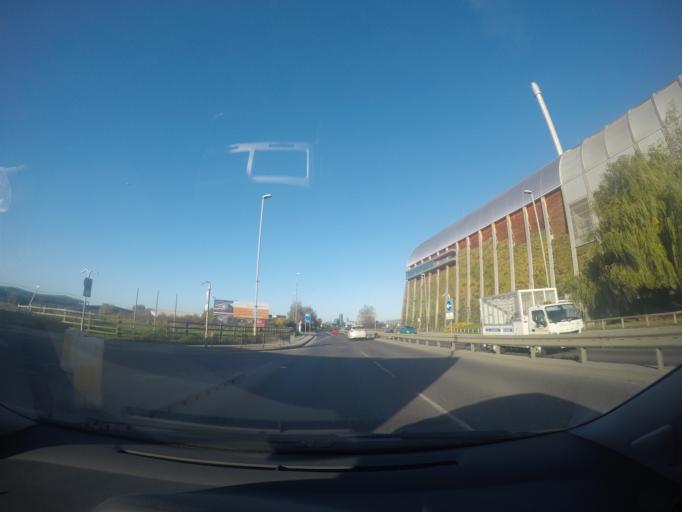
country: GB
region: England
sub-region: City and Borough of Leeds
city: Leeds
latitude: 53.7867
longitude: -1.5028
